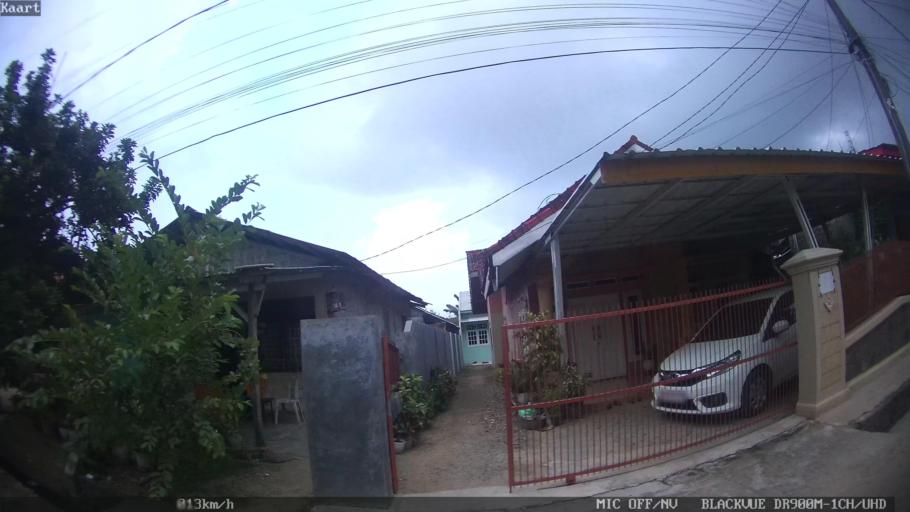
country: ID
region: Lampung
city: Bandarlampung
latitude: -5.4086
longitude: 105.2791
